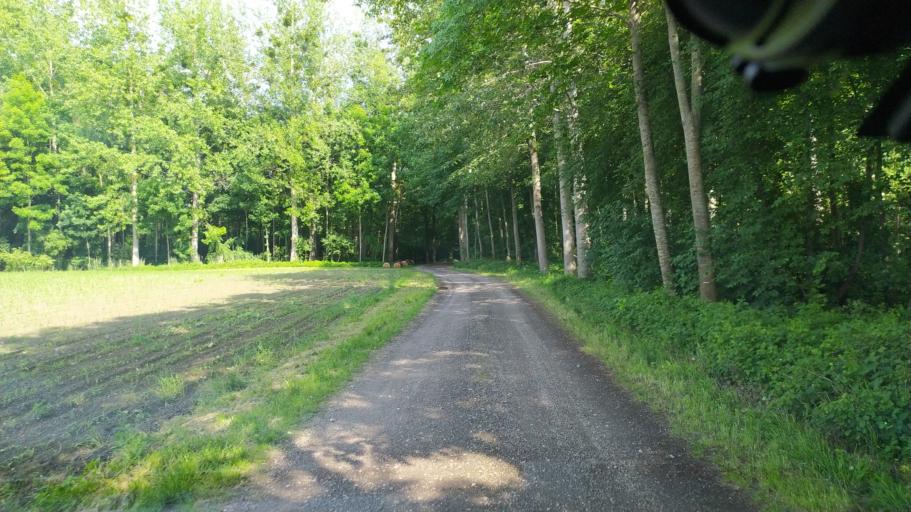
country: AT
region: Lower Austria
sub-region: Politischer Bezirk Amstetten
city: Strengberg
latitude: 48.1743
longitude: 14.6826
